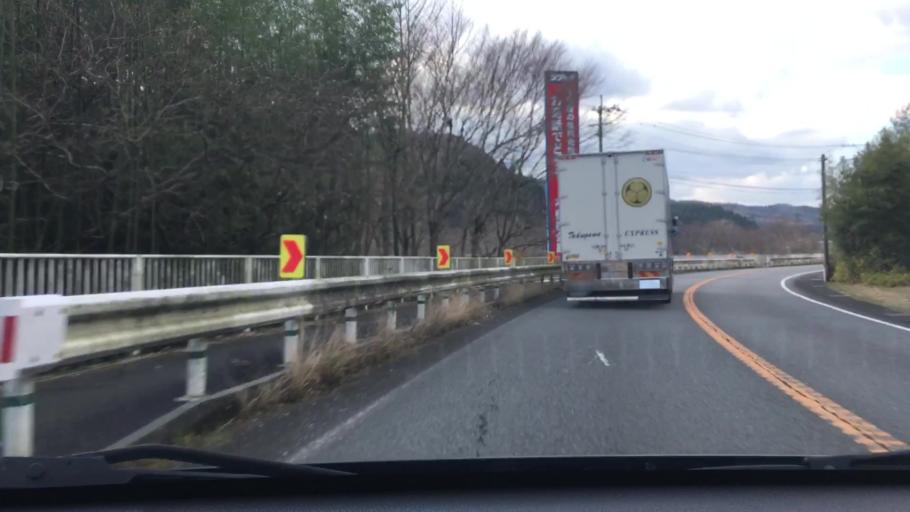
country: JP
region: Oita
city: Usuki
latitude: 33.0048
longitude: 131.7281
